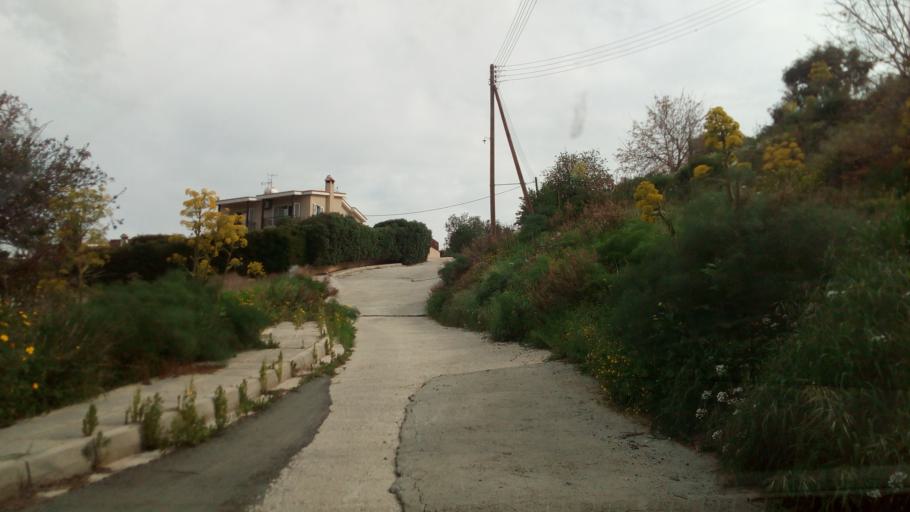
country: CY
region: Pafos
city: Mesogi
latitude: 34.7972
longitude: 32.4746
